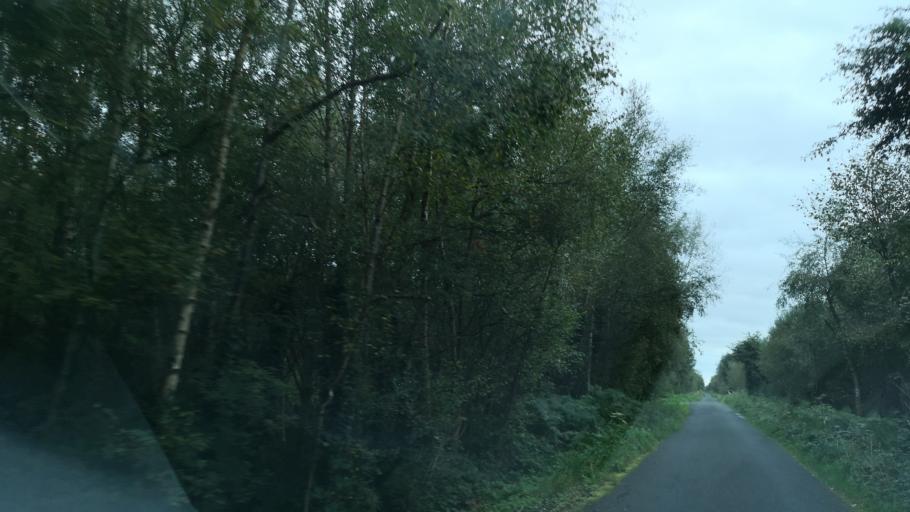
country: IE
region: Leinster
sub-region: Uibh Fhaili
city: Ferbane
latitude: 53.2013
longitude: -7.7249
